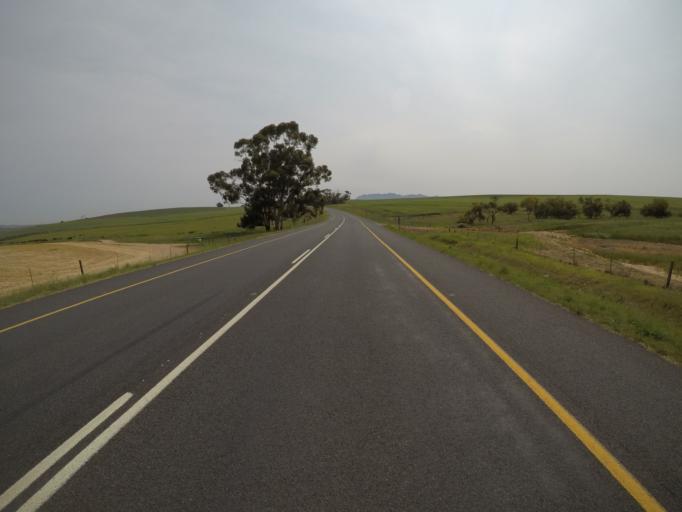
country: ZA
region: Western Cape
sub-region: West Coast District Municipality
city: Malmesbury
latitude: -33.5154
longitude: 18.8459
